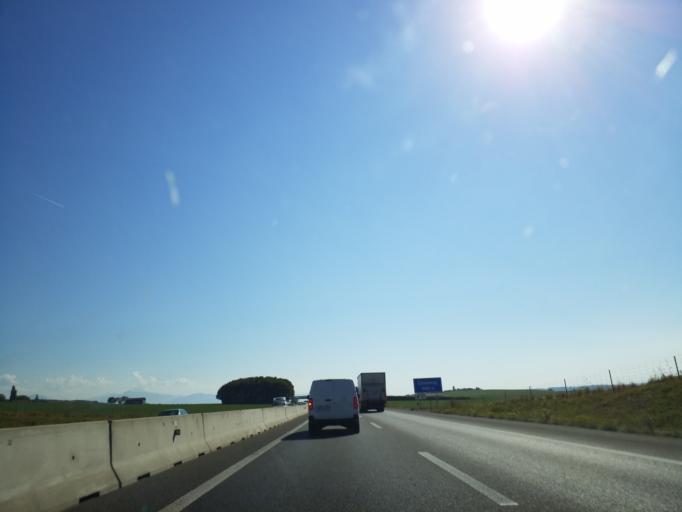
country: CH
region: Vaud
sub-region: Gros-de-Vaud District
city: Penthalaz
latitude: 46.6119
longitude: 6.5565
